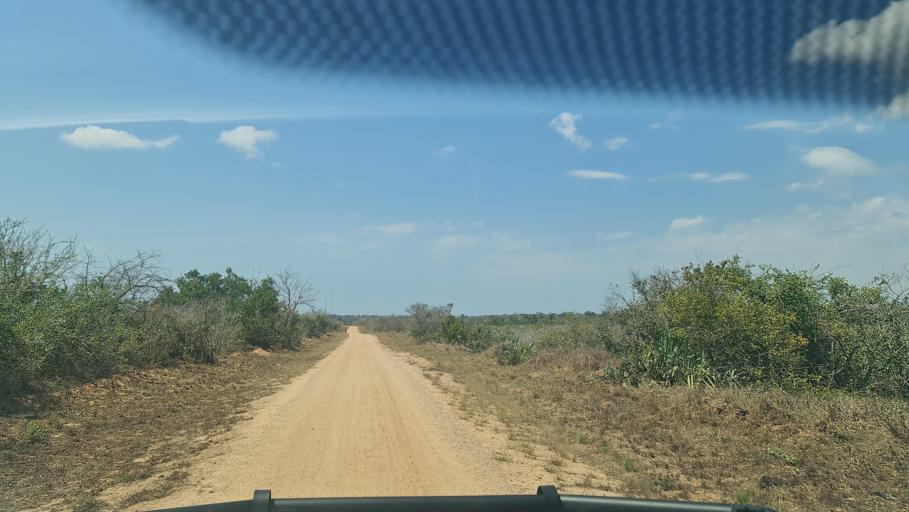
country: MZ
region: Nampula
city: Ilha de Mocambique
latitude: -15.1844
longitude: 40.5173
